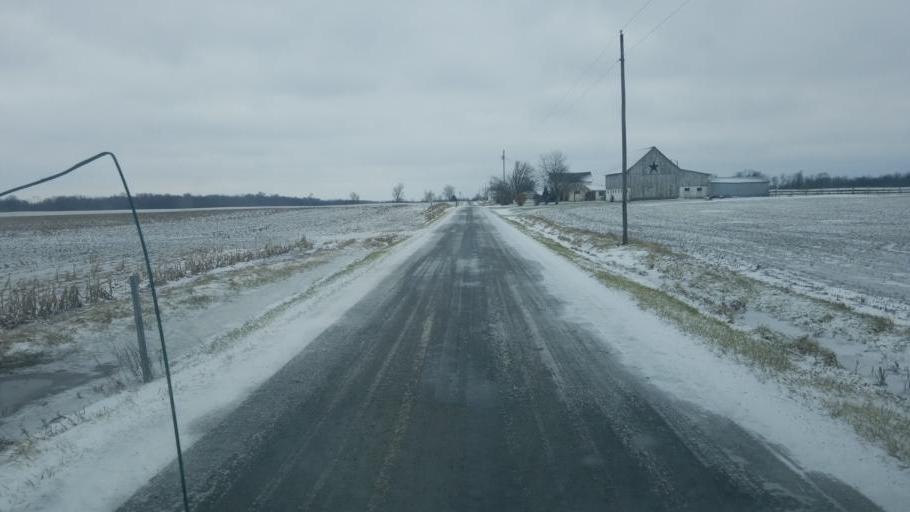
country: US
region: Ohio
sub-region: Delaware County
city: Sunbury
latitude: 40.2316
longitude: -82.7688
